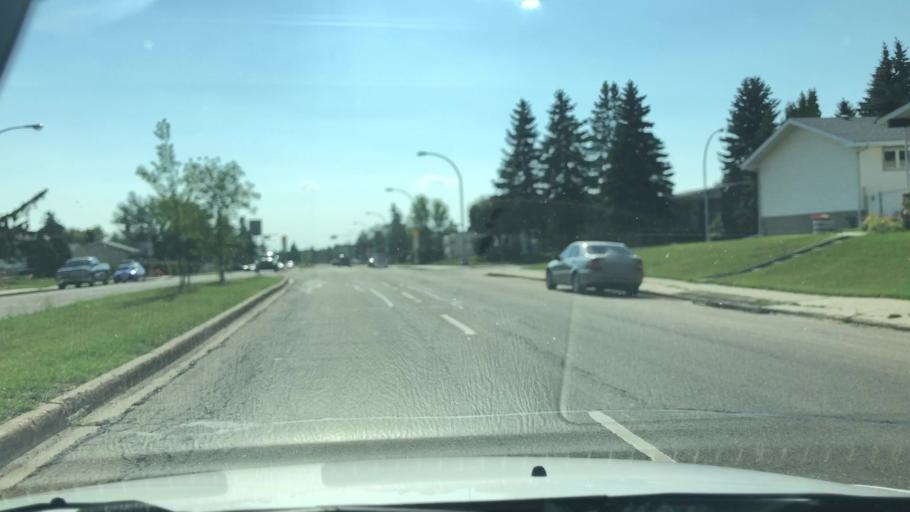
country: CA
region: Alberta
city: Edmonton
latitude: 53.6068
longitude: -113.4716
